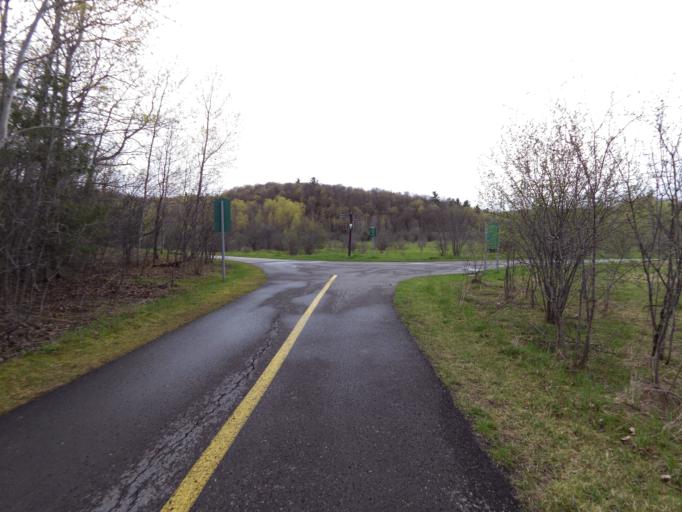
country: CA
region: Quebec
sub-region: Outaouais
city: Gatineau
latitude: 45.4647
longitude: -75.7869
